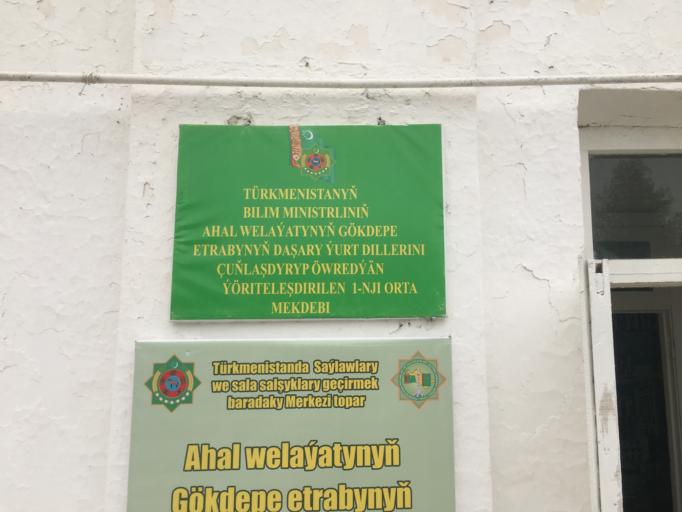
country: TM
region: Ahal
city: Abadan
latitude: 38.1544
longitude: 57.9622
